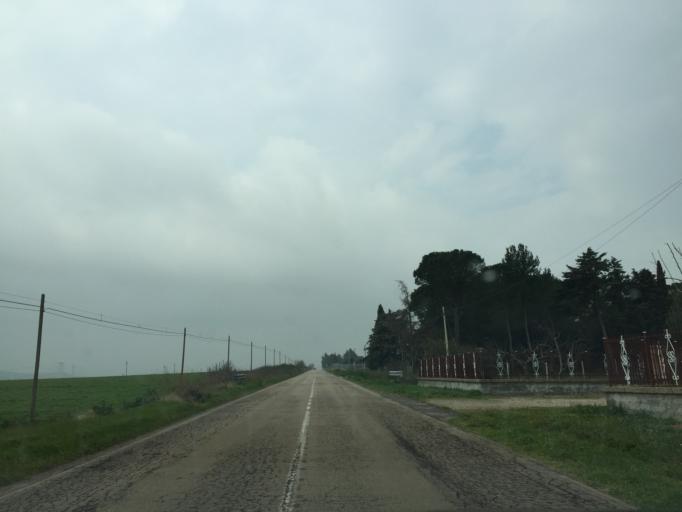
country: IT
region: Apulia
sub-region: Provincia di Foggia
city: Troia
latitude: 41.3914
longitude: 15.4060
